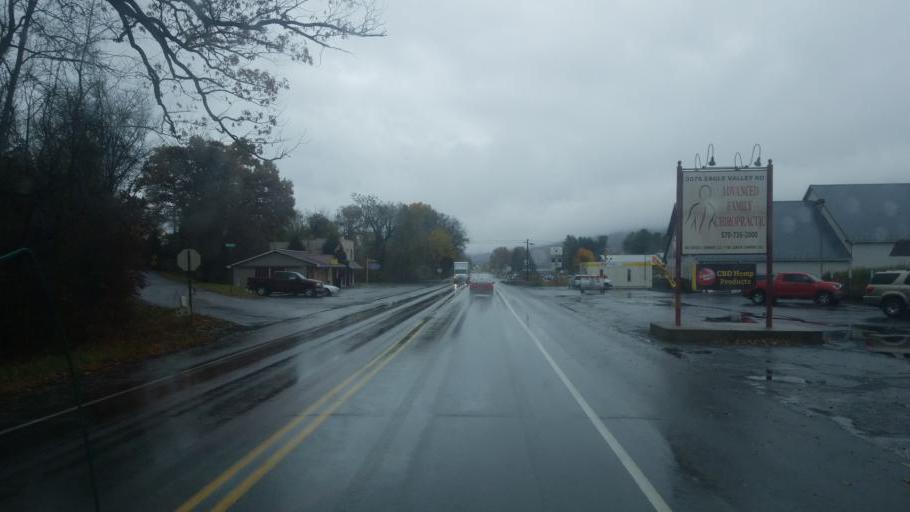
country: US
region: Pennsylvania
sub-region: Clinton County
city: Mill Hall
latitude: 41.1127
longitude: -77.4927
